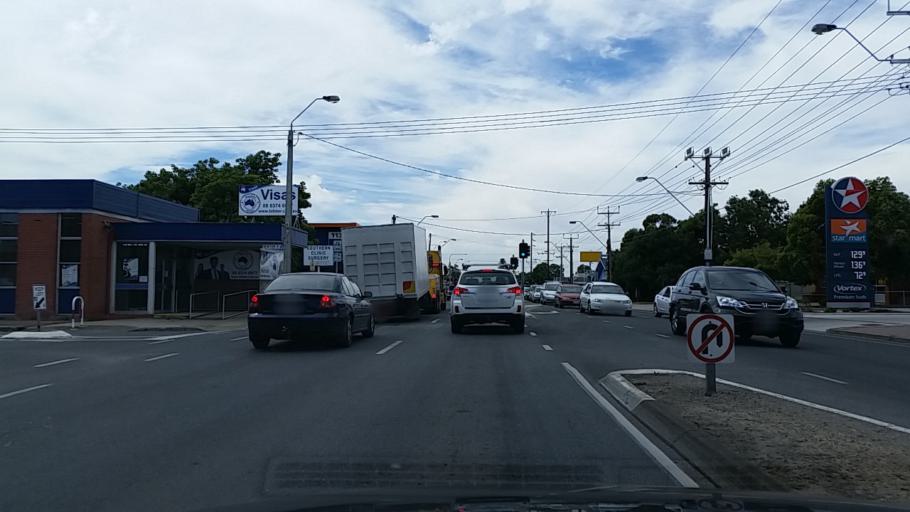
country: AU
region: South Australia
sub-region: Marion
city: Clovelly Park
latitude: -34.9946
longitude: 138.5750
